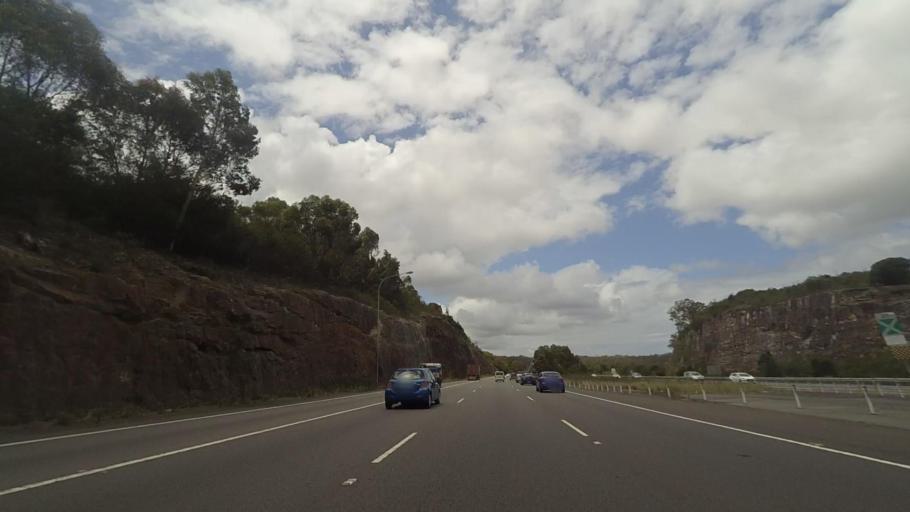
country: AU
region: New South Wales
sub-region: Gosford Shire
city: Point Clare
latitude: -33.4526
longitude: 151.2097
